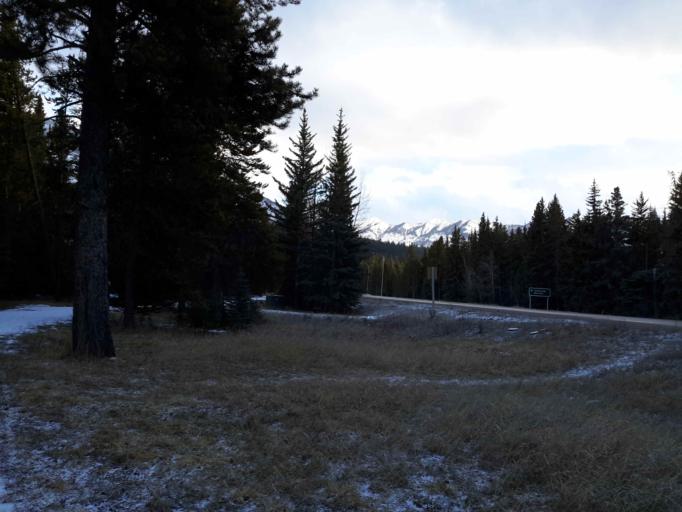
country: CA
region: Alberta
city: Banff
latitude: 51.2027
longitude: -115.5371
